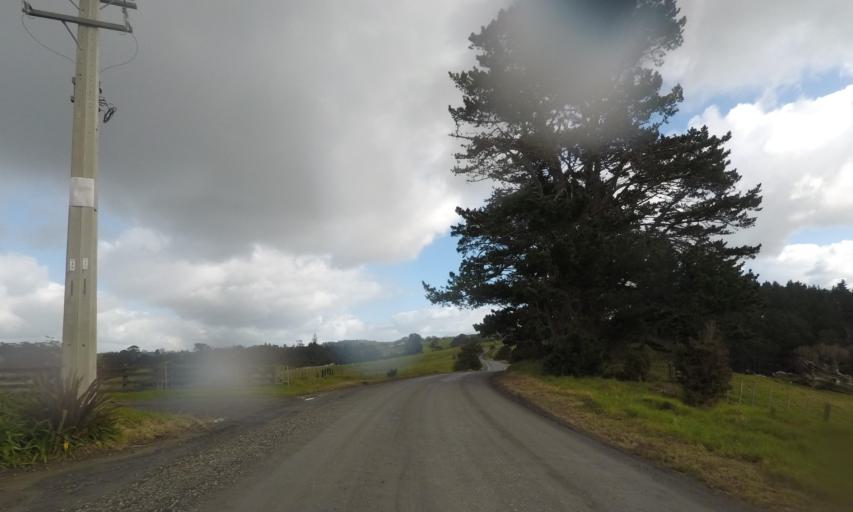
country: NZ
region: Auckland
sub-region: Auckland
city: Wellsford
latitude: -36.1737
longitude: 174.5970
